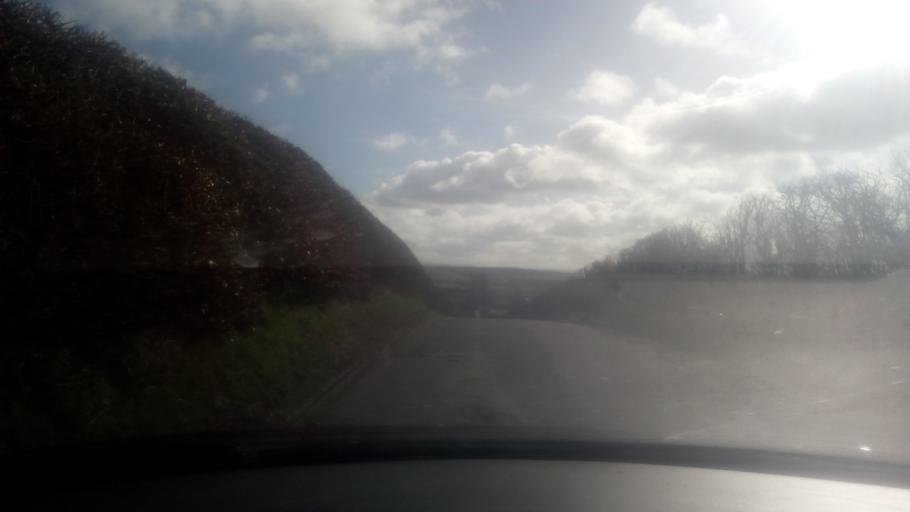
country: GB
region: Scotland
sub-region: The Scottish Borders
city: Saint Boswells
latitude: 55.5341
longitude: -2.6482
